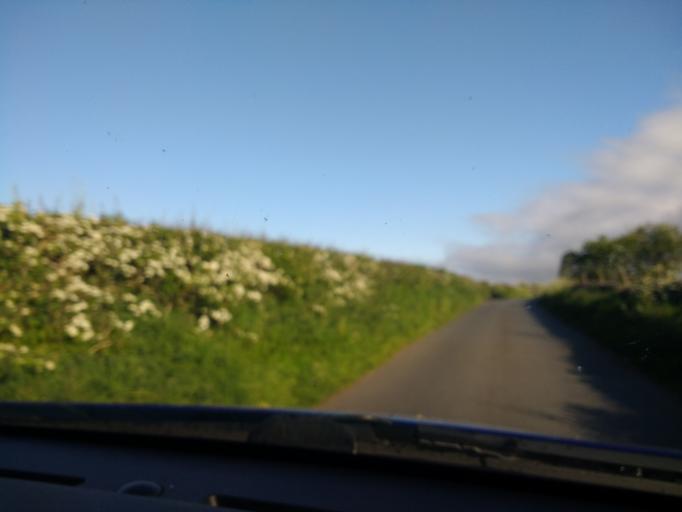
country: GB
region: England
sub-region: Cumbria
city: Appleby-in-Westmorland
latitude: 54.6769
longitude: -2.5798
